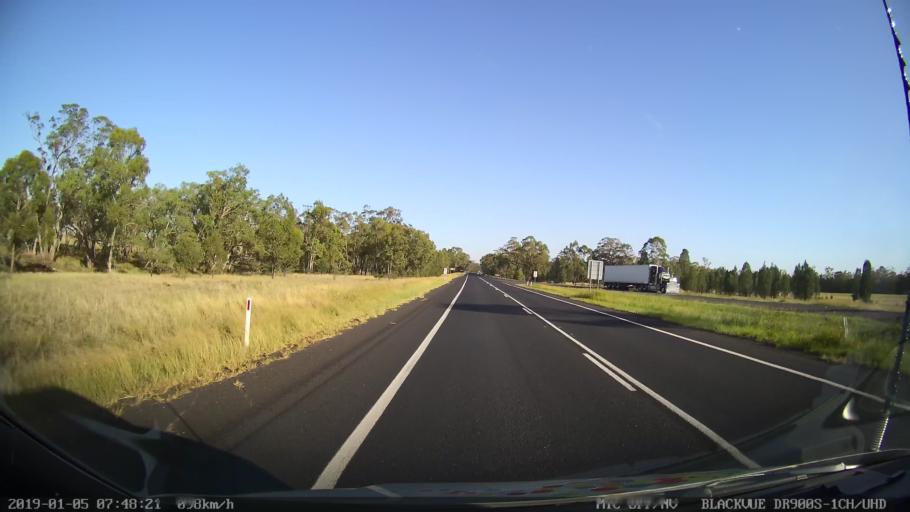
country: AU
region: New South Wales
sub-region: Gilgandra
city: Gilgandra
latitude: -31.8176
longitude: 148.6387
